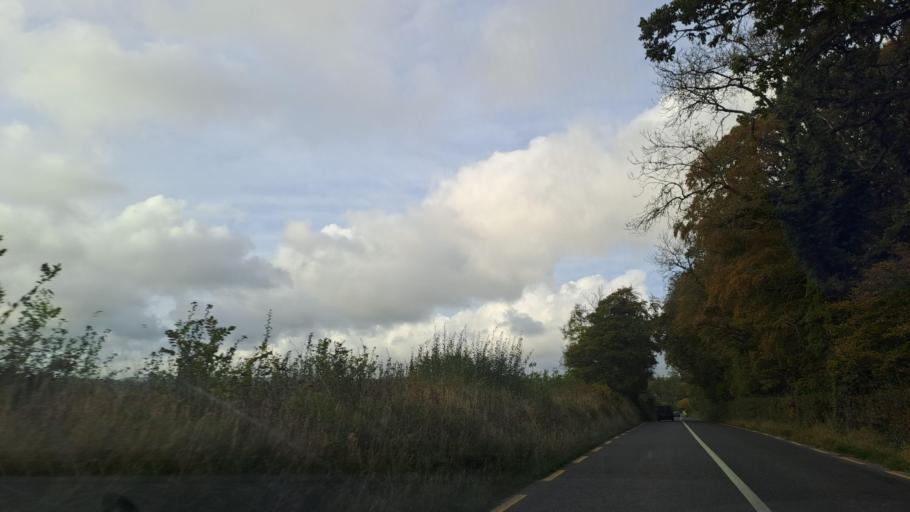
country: IE
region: Ulster
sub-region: An Cabhan
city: Kingscourt
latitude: 53.8550
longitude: -6.7810
